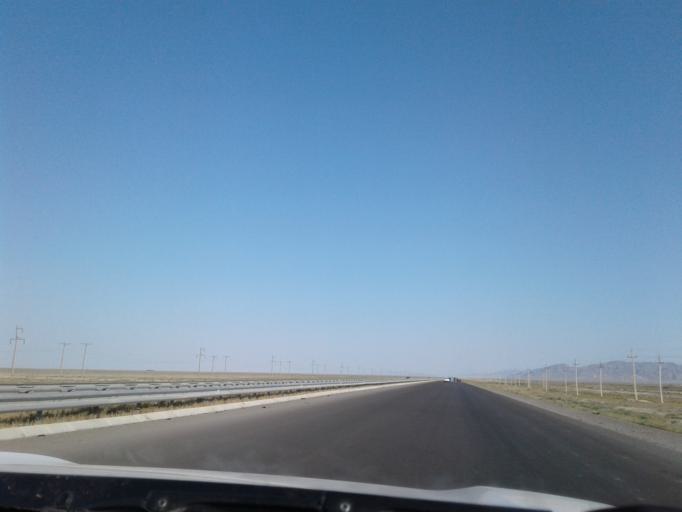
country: TM
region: Balkan
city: Gazanjyk
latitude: 39.1461
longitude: 55.8628
